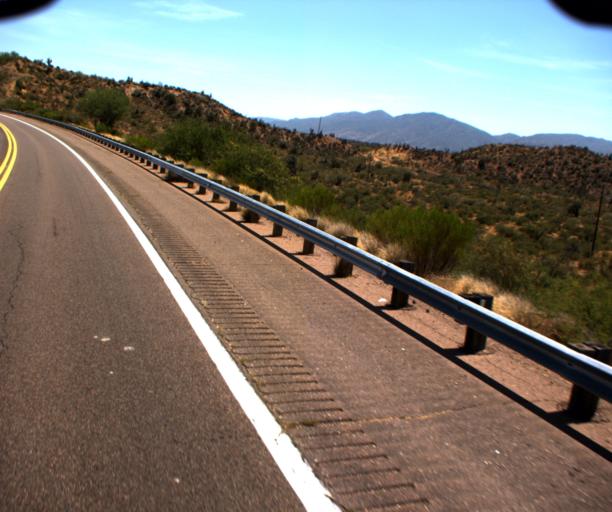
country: US
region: Arizona
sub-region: Gila County
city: Tonto Basin
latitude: 33.9216
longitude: -111.3181
